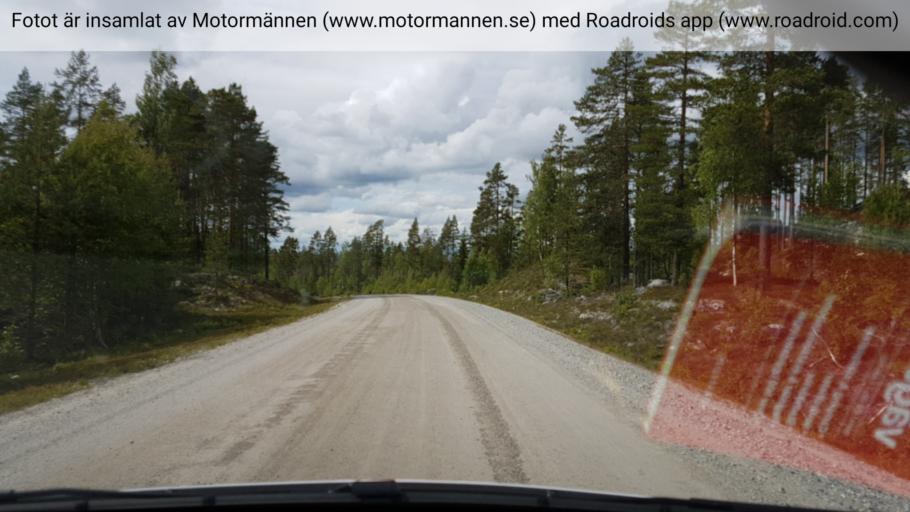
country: SE
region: Vaesternorrland
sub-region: Solleftea Kommun
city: Solleftea
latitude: 63.3242
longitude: 17.3662
